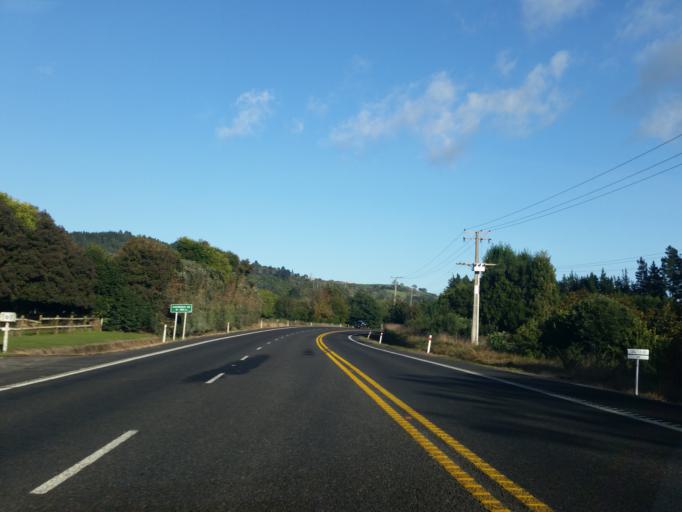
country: NZ
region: Bay of Plenty
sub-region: Tauranga City
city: Tauranga
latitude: -37.6973
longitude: 176.0595
